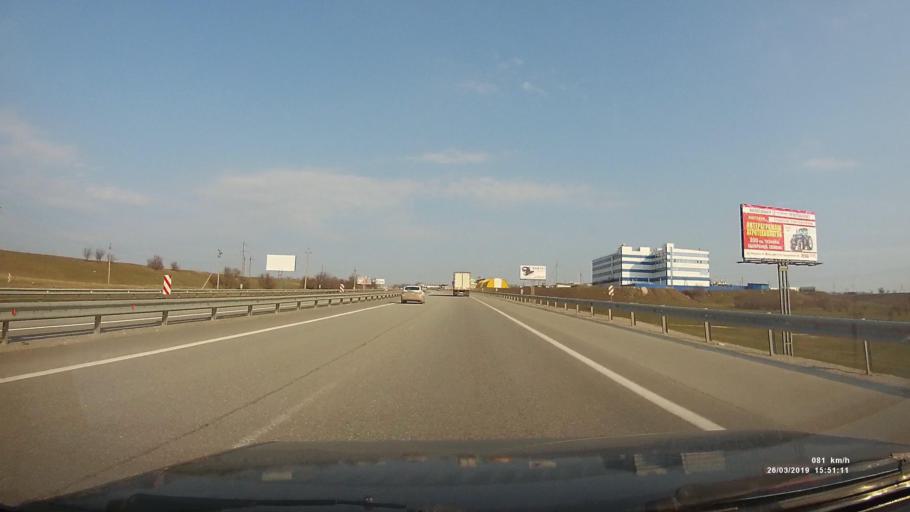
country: RU
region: Rostov
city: Chaltyr
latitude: 47.2701
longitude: 39.4999
